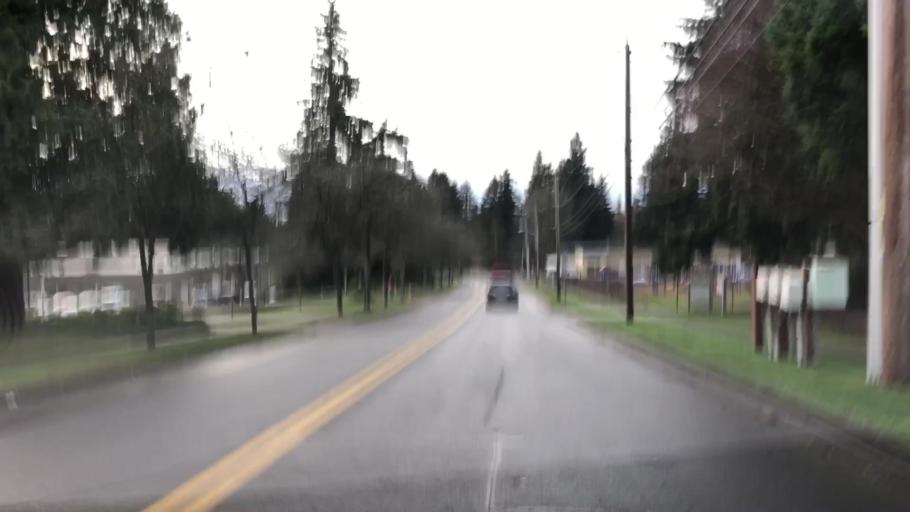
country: US
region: Washington
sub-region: King County
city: Yarrow Point
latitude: 47.6559
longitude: -122.1938
